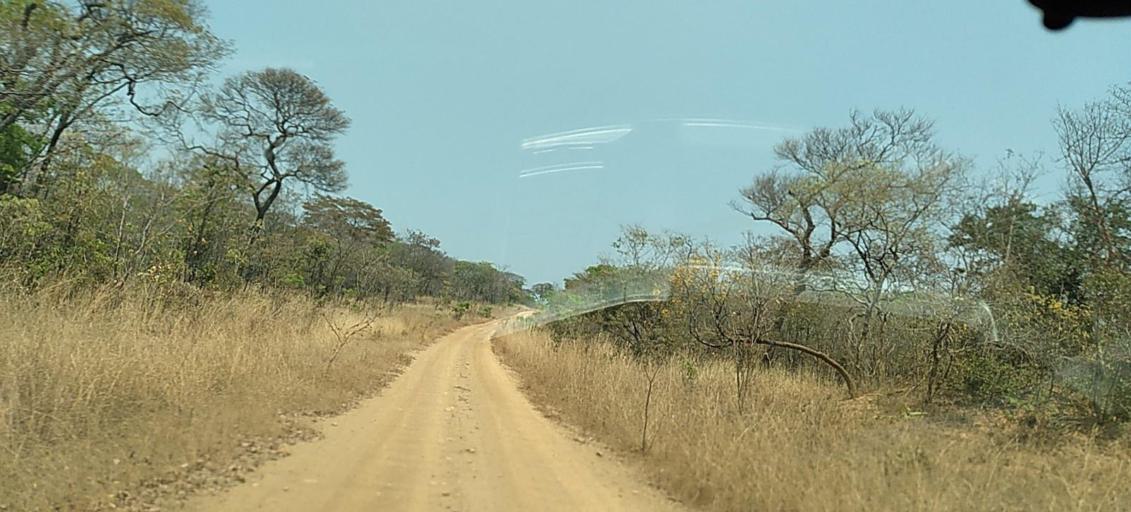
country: ZM
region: Central
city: Mumbwa
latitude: -14.4159
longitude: 26.4892
